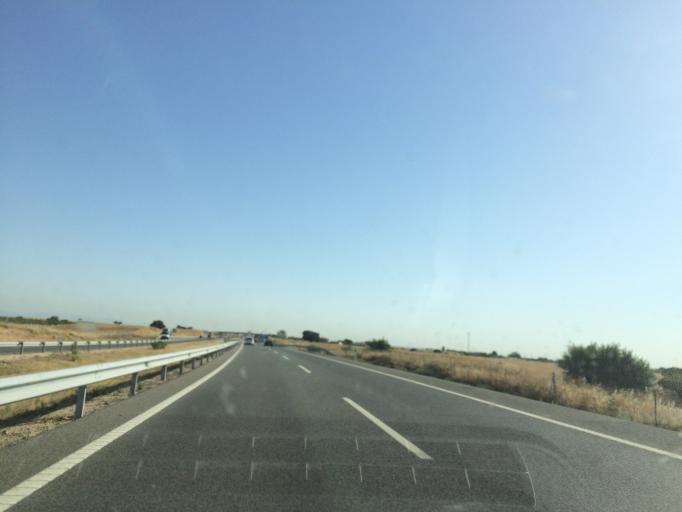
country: ES
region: Castille-La Mancha
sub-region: Province of Toledo
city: La Torre de Esteban Hambran
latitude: 40.1500
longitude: -4.1783
